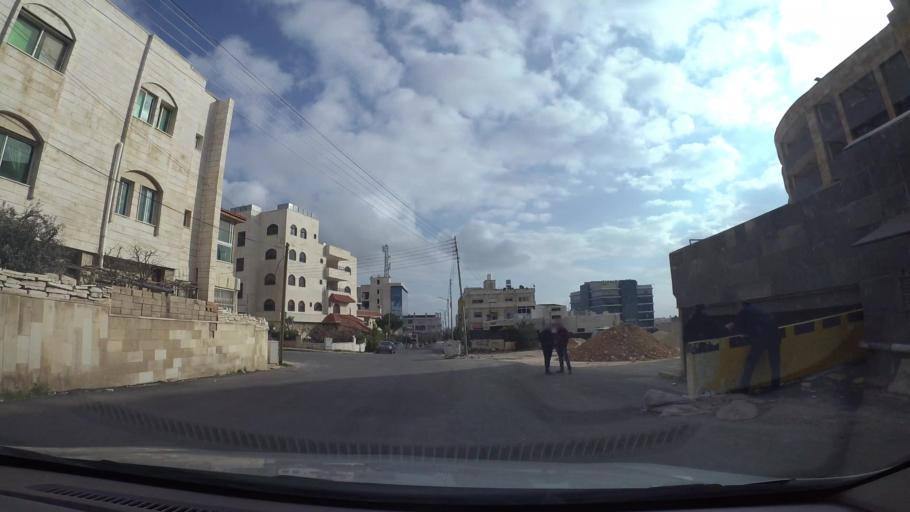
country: JO
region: Amman
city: Wadi as Sir
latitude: 31.9769
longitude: 35.8446
